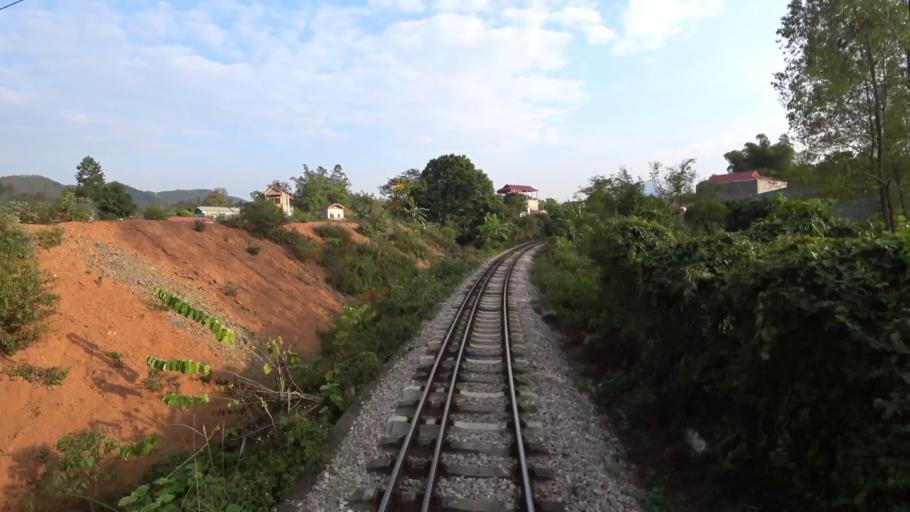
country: VN
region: Lang Son
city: Thi Tran Cao Loc
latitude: 21.9336
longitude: 106.6990
